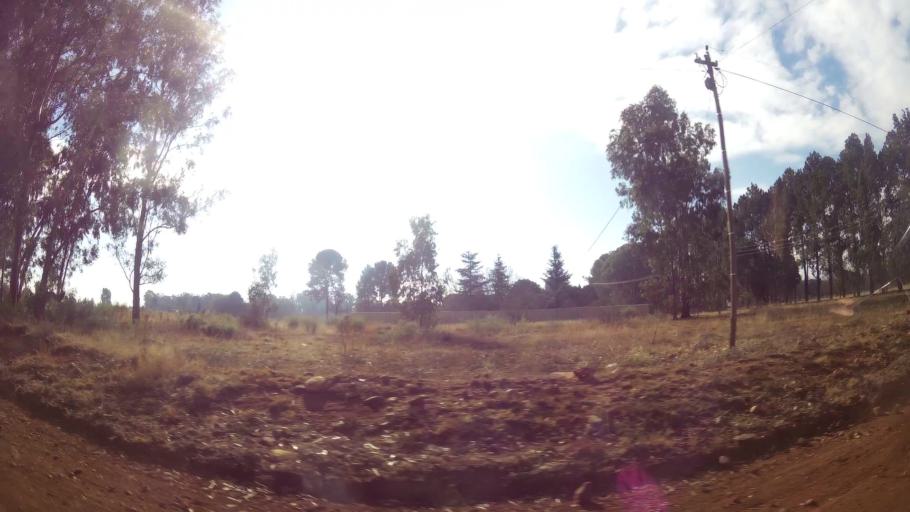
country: ZA
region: Gauteng
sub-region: Sedibeng District Municipality
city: Meyerton
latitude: -26.5502
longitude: 28.0506
